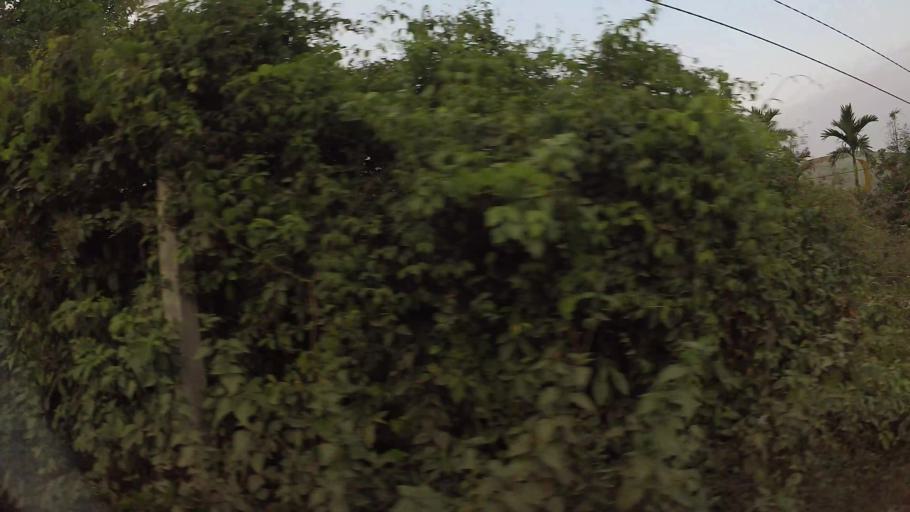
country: VN
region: Da Nang
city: Lien Chieu
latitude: 16.0532
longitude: 108.1092
